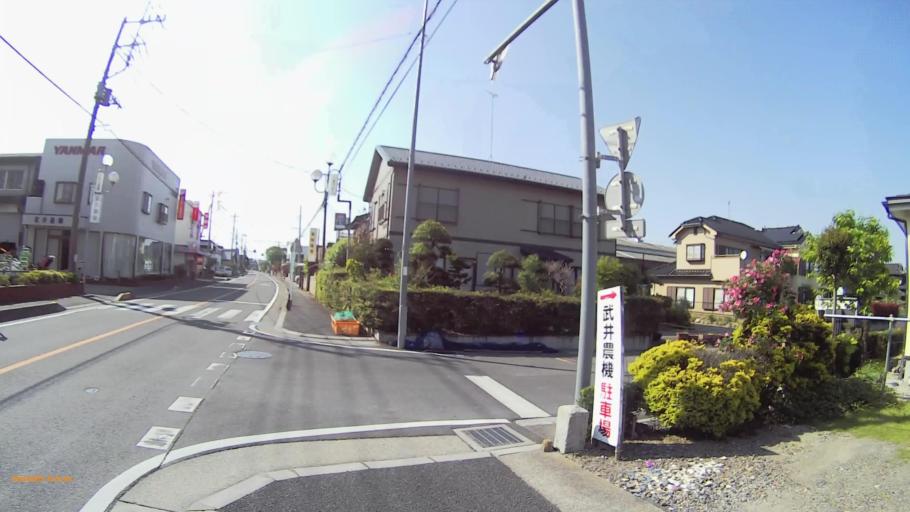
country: JP
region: Saitama
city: Sugito
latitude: 36.0227
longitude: 139.7406
